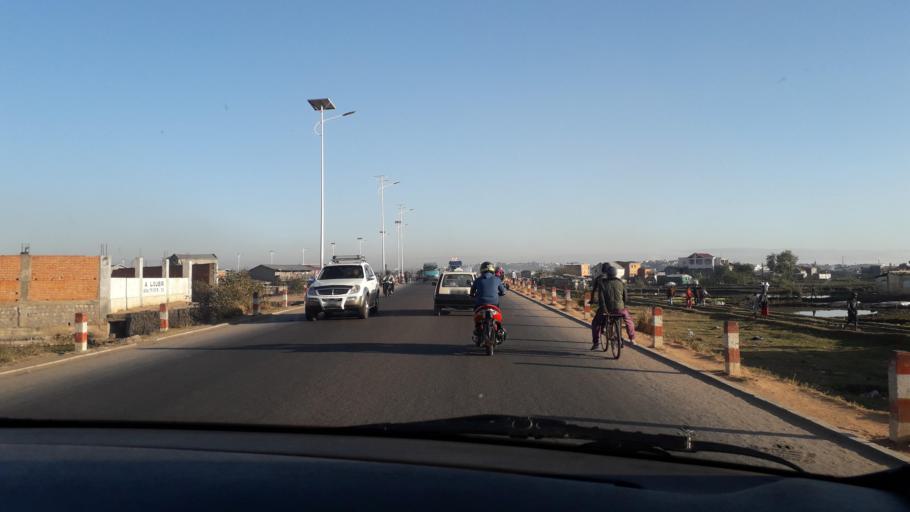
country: MG
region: Analamanga
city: Antananarivo
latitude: -18.8955
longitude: 47.5101
